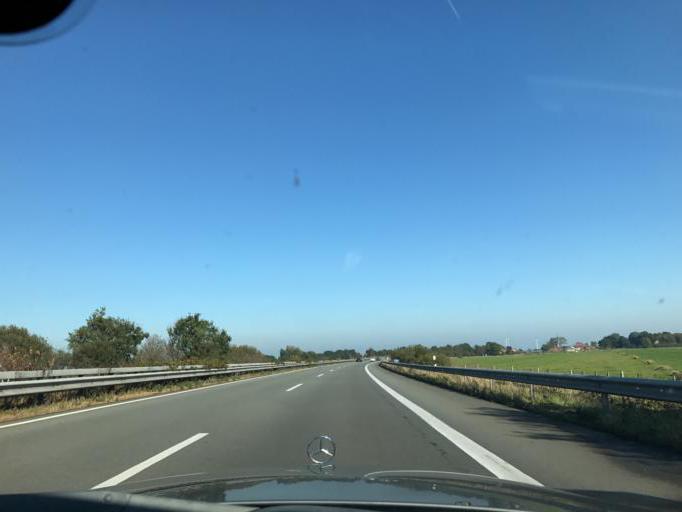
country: DE
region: Lower Saxony
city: Bunde
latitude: 53.2079
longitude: 7.3119
